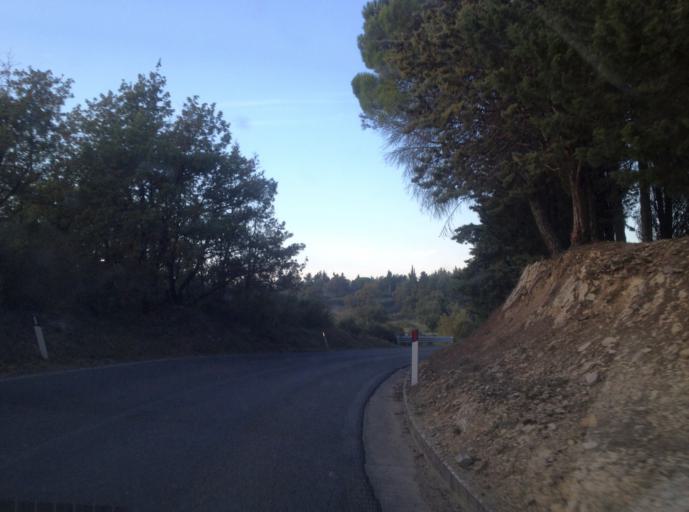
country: IT
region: Tuscany
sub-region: Provincia di Siena
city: Castellina in Chianti
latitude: 43.4483
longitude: 11.2956
